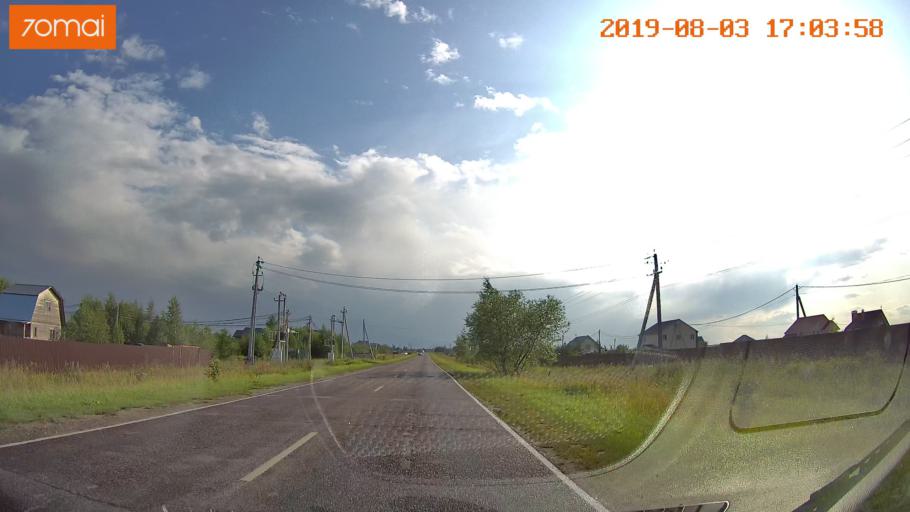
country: RU
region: Moskovskaya
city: Troitskoye
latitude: 55.3324
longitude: 38.5638
